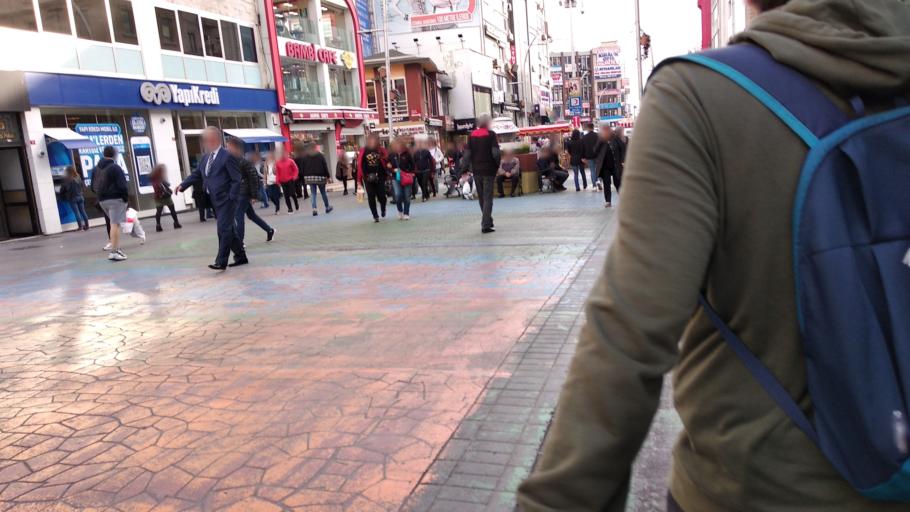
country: TR
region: Istanbul
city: Bahcelievler
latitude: 40.9796
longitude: 28.8741
